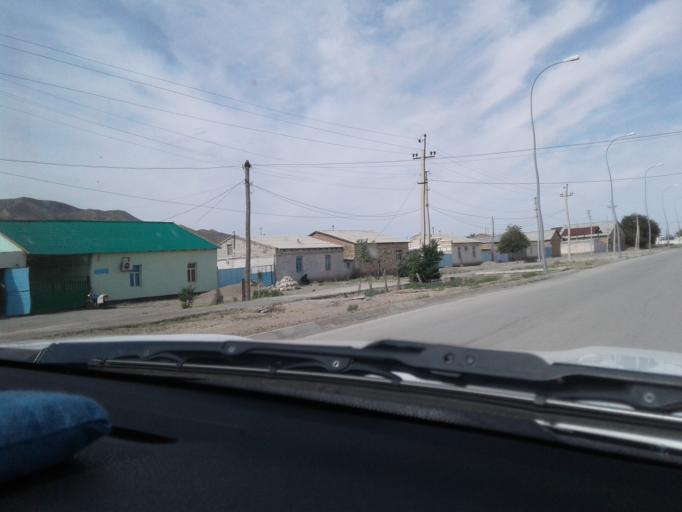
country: TM
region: Balkan
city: Gazanjyk
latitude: 39.2452
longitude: 55.5024
